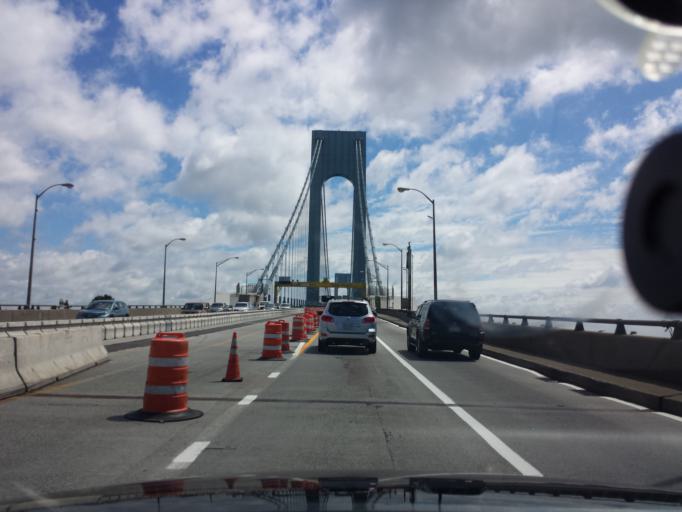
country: US
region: New York
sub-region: Kings County
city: Bensonhurst
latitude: 40.6022
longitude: -74.0580
